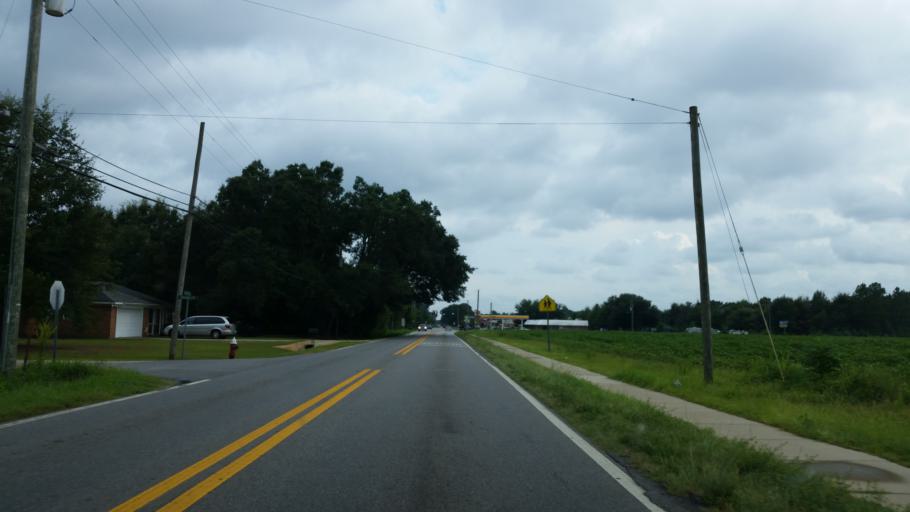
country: US
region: Florida
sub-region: Santa Rosa County
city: Pace
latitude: 30.6169
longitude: -87.1486
